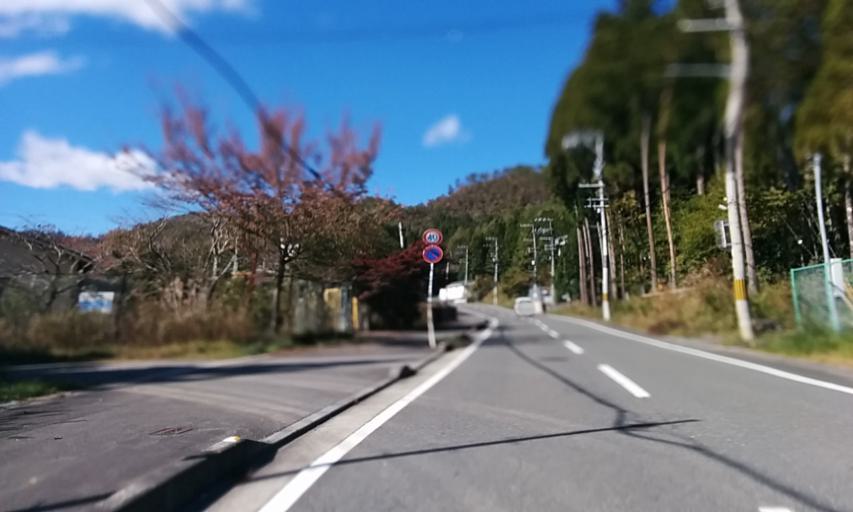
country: JP
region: Kyoto
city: Kameoka
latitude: 35.1987
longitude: 135.6317
